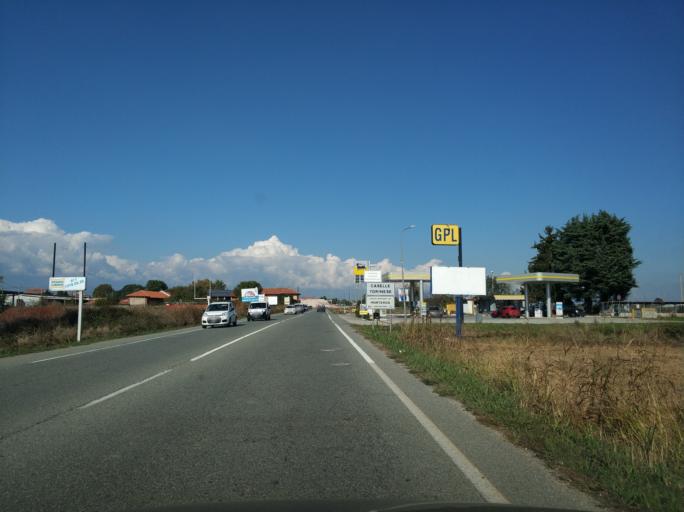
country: IT
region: Piedmont
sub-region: Provincia di Torino
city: Borgaro Torinese
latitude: 45.1618
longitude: 7.6548
